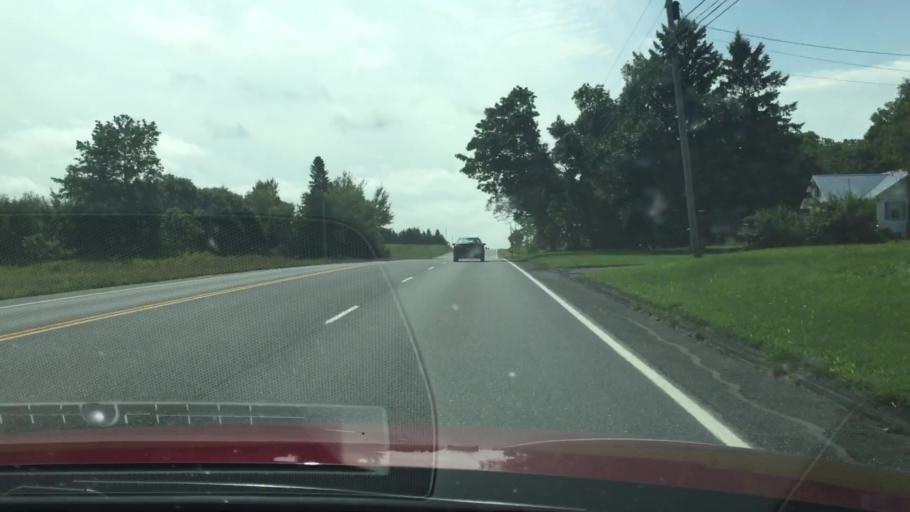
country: CA
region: New Brunswick
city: Florenceville-Bristol
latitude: 46.3959
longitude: -67.8430
